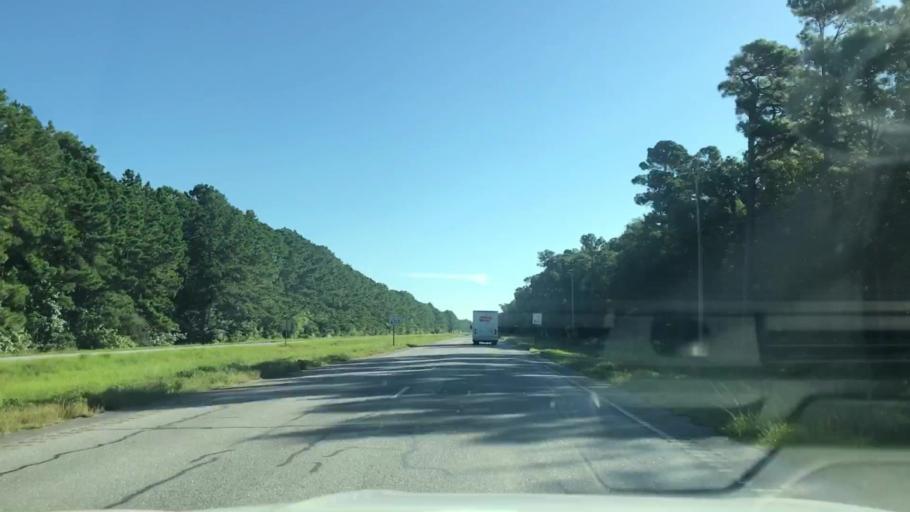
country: US
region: South Carolina
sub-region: Charleston County
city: Awendaw
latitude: 33.0633
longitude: -79.5341
